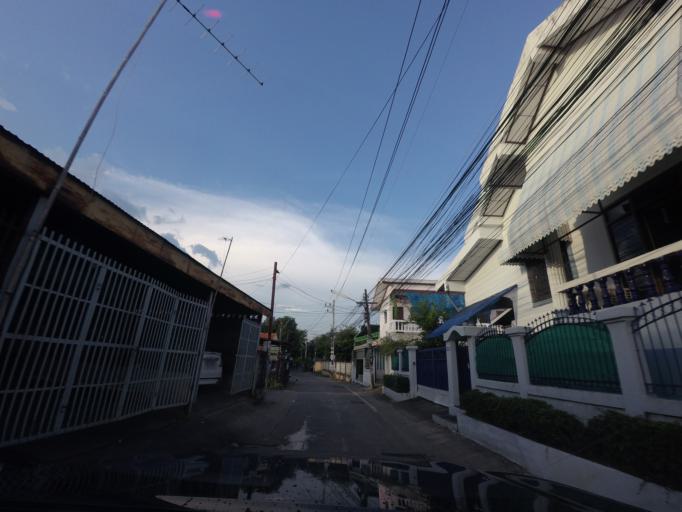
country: TH
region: Khon Kaen
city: Khon Kaen
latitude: 16.4325
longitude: 102.8568
